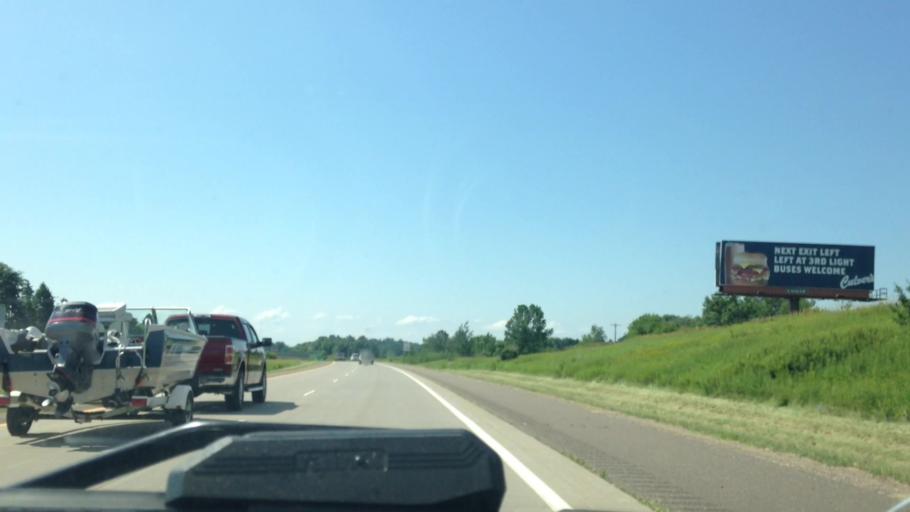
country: US
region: Wisconsin
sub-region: Barron County
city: Rice Lake
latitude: 45.5009
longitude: -91.7642
